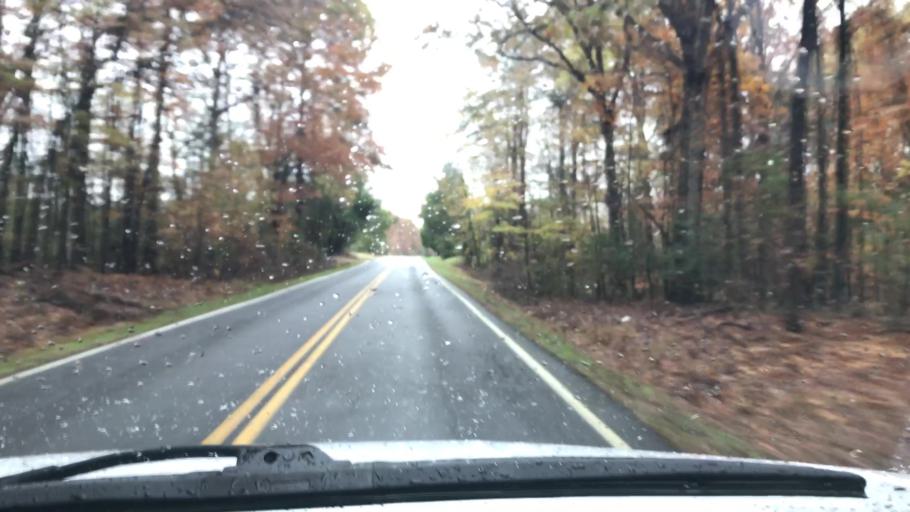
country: US
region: Virginia
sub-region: Henrico County
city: Short Pump
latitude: 37.6183
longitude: -77.6951
